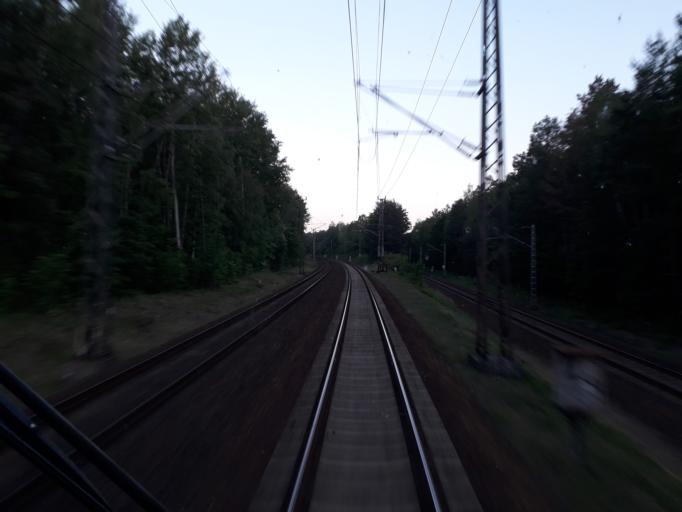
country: DE
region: Brandenburg
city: Birkenwerder
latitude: 52.6743
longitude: 13.3064
